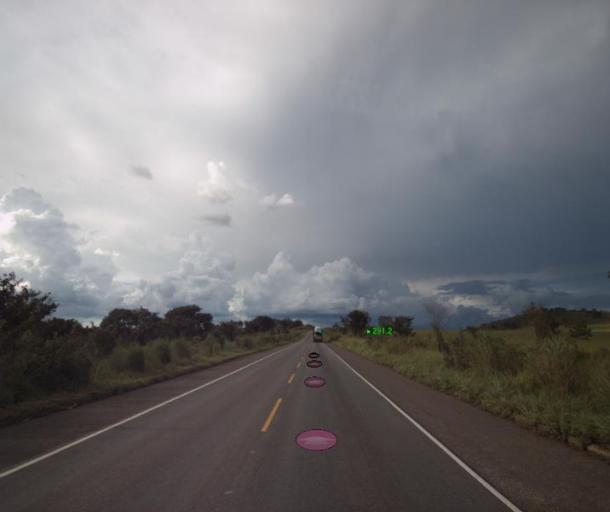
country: BR
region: Goias
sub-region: Ceres
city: Ceres
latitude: -15.2307
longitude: -49.5549
